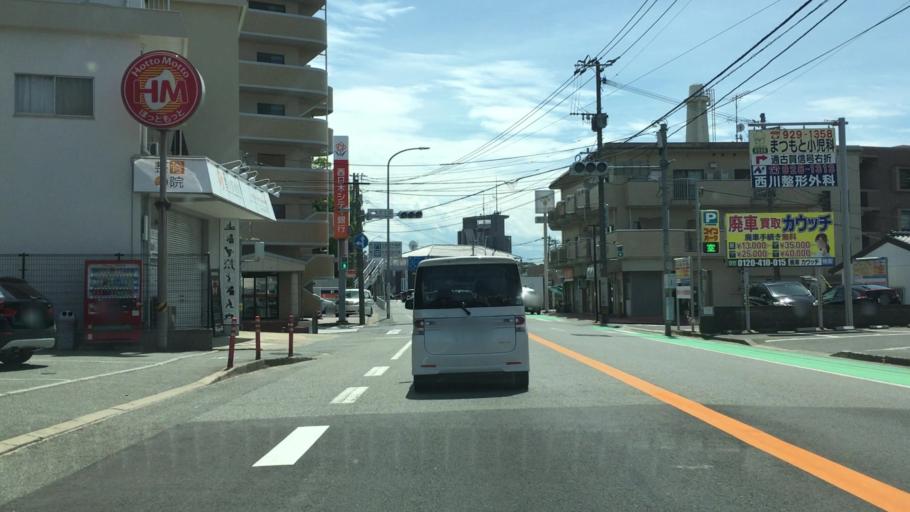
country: JP
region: Fukuoka
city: Dazaifu
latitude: 33.5142
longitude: 130.5069
